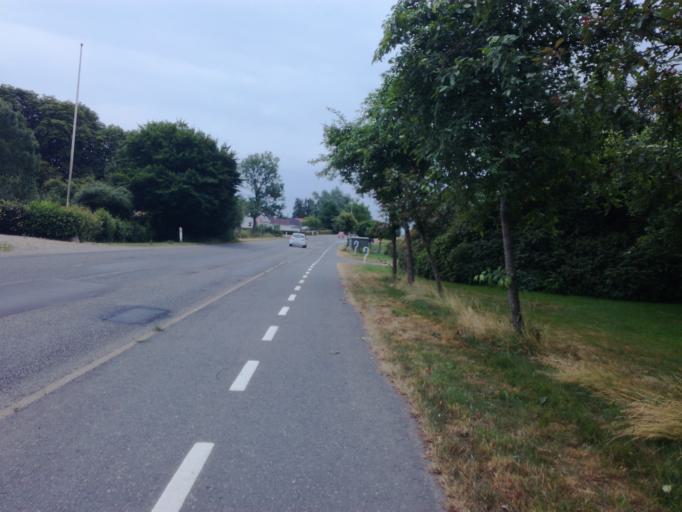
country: DK
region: South Denmark
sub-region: Vejle Kommune
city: Borkop
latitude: 55.6679
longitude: 9.6234
